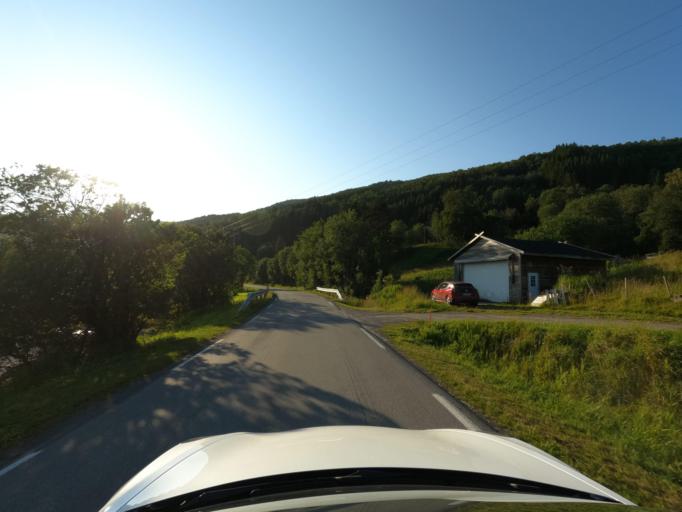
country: NO
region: Nordland
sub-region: Ballangen
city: Ballangen
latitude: 68.4679
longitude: 16.8115
